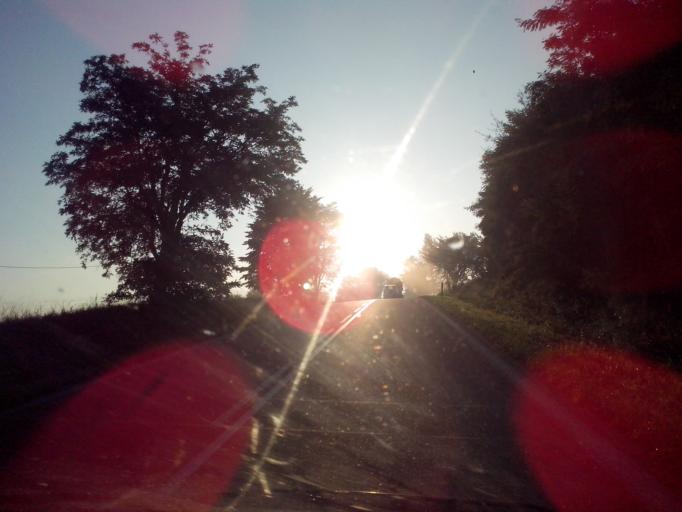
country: PL
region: Subcarpathian Voivodeship
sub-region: Powiat strzyzowski
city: Gwoznica Gorna
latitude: 49.8101
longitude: 22.0080
